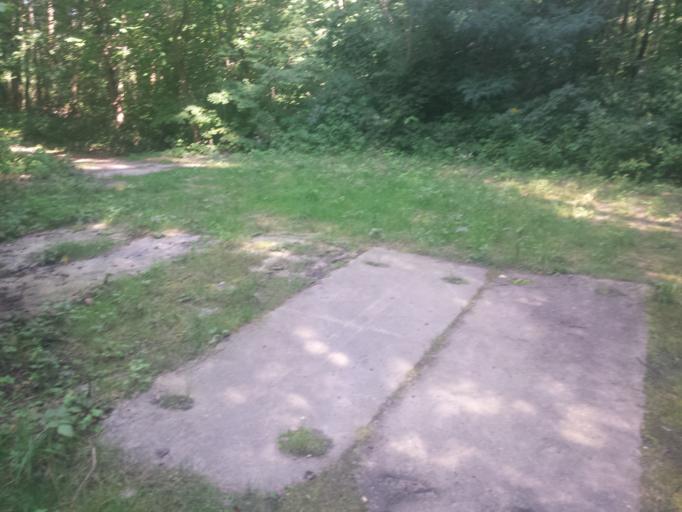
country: DE
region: Saxony
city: Taucha
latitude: 51.3908
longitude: 12.4794
